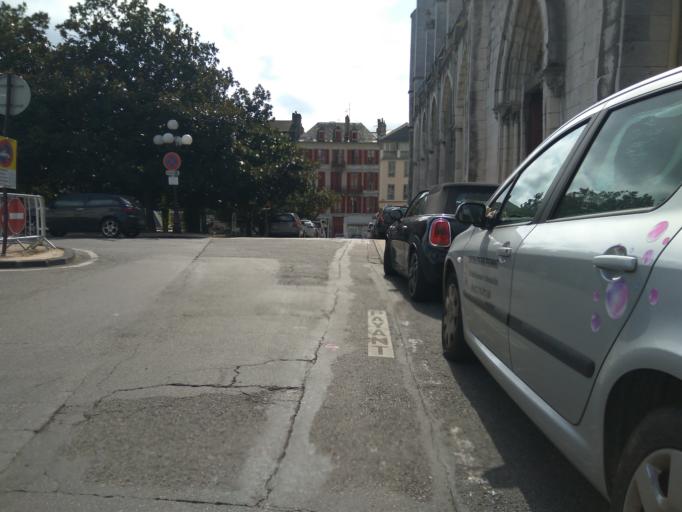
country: FR
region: Aquitaine
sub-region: Departement des Pyrenees-Atlantiques
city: Pau
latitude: 43.2982
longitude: -0.3722
